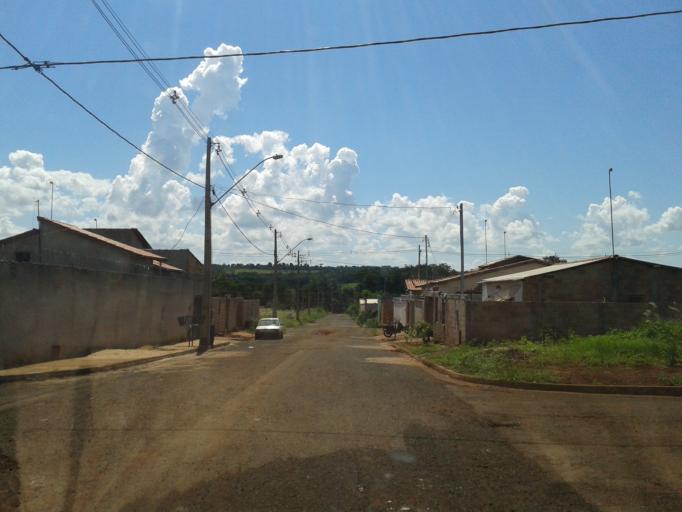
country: BR
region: Goias
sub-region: Itumbiara
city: Itumbiara
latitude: -18.4229
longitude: -49.1851
